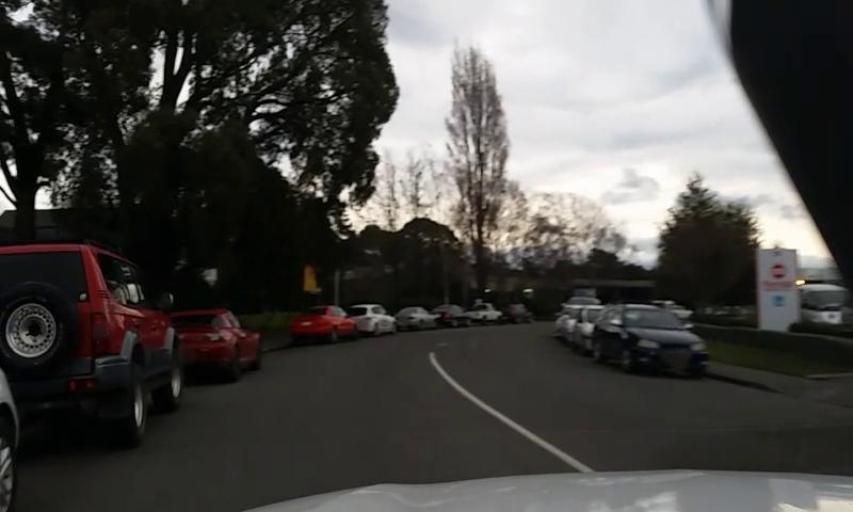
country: NZ
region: Canterbury
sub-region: Christchurch City
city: Christchurch
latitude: -43.4915
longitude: 172.5612
